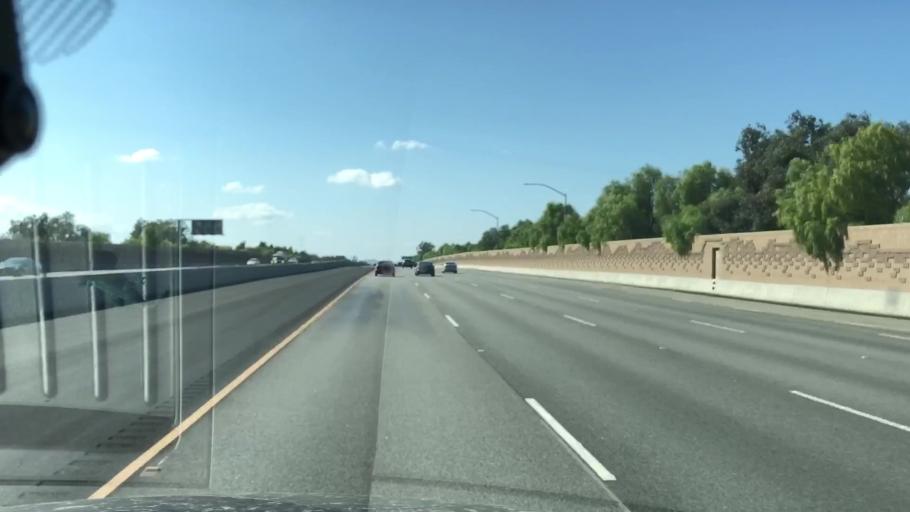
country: US
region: California
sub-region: Ventura County
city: Santa Susana
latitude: 34.2818
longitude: -118.6947
